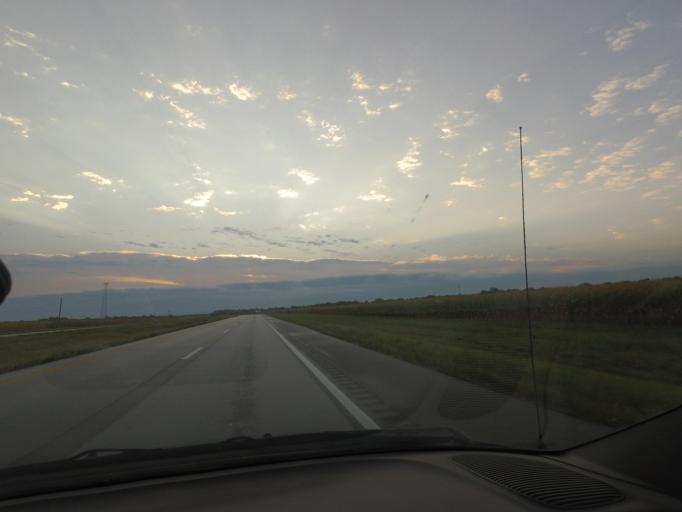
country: US
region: Missouri
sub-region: Macon County
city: Macon
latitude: 39.7502
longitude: -92.2757
